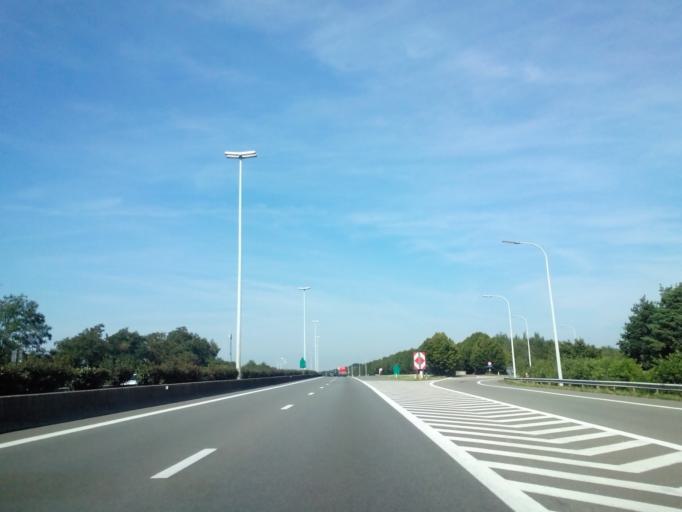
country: BE
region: Flanders
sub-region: Provincie Vlaams-Brabant
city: Aarschot
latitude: 50.9643
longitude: 4.8427
